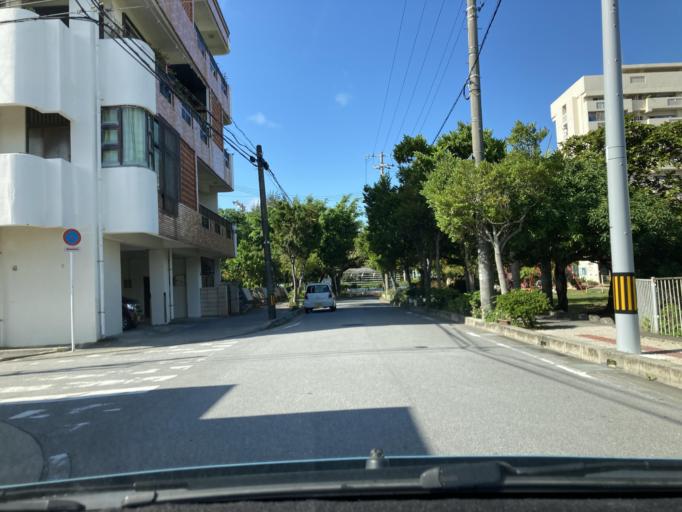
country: JP
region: Okinawa
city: Naha-shi
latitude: 26.2232
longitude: 127.6783
